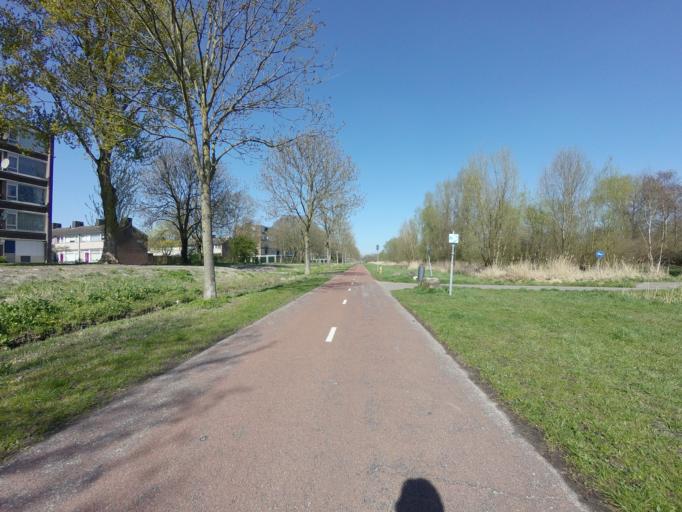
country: NL
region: North Holland
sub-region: Gemeente Haarlem
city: Haarlem
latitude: 52.3618
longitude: 4.6676
